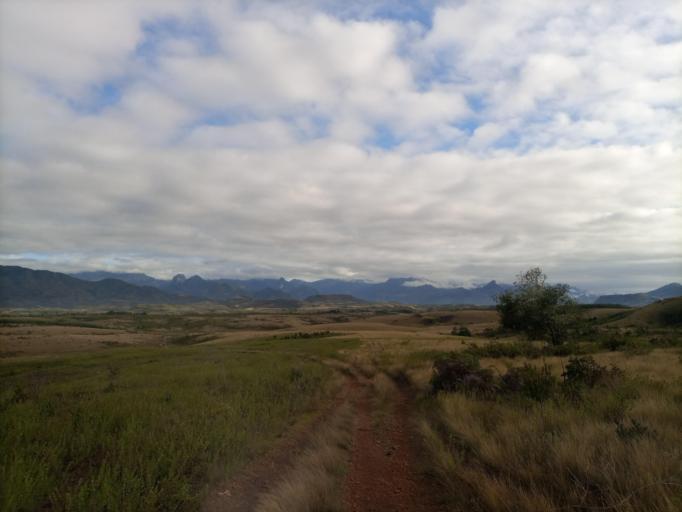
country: MG
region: Anosy
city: Fort Dauphin
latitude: -24.3092
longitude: 47.2483
